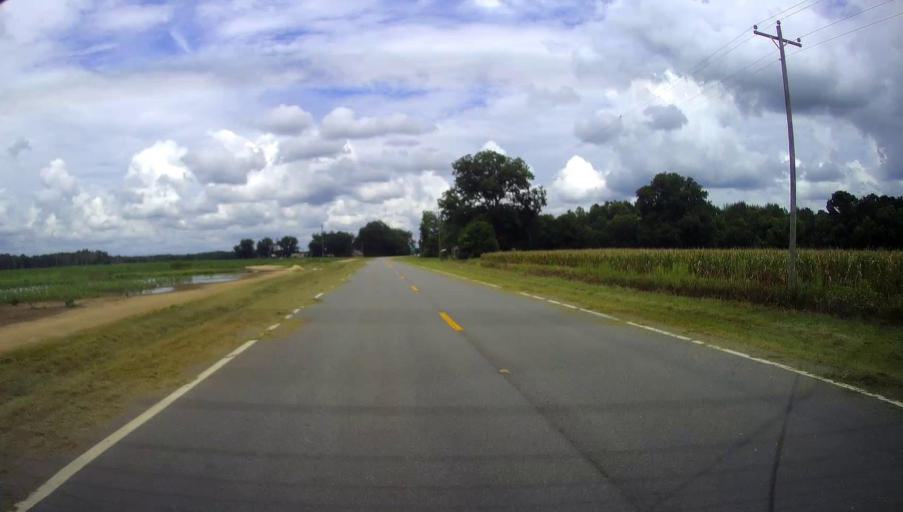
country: US
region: Georgia
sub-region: Macon County
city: Oglethorpe
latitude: 32.2784
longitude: -84.1759
